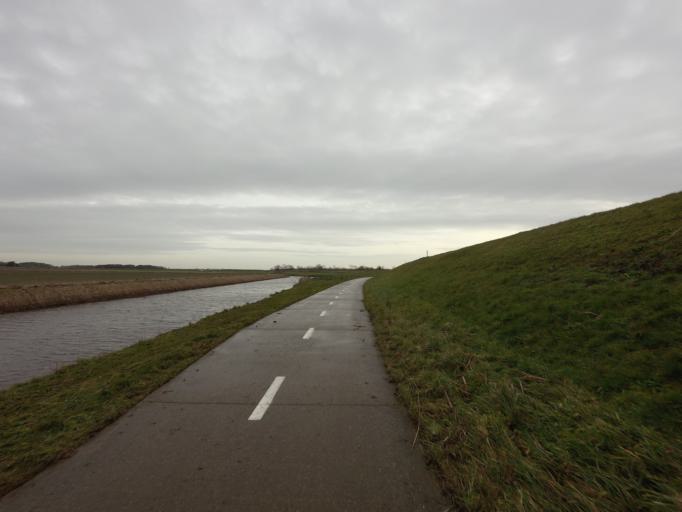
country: NL
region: North Holland
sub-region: Gemeente Texel
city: Den Burg
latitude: 53.0300
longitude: 4.8061
